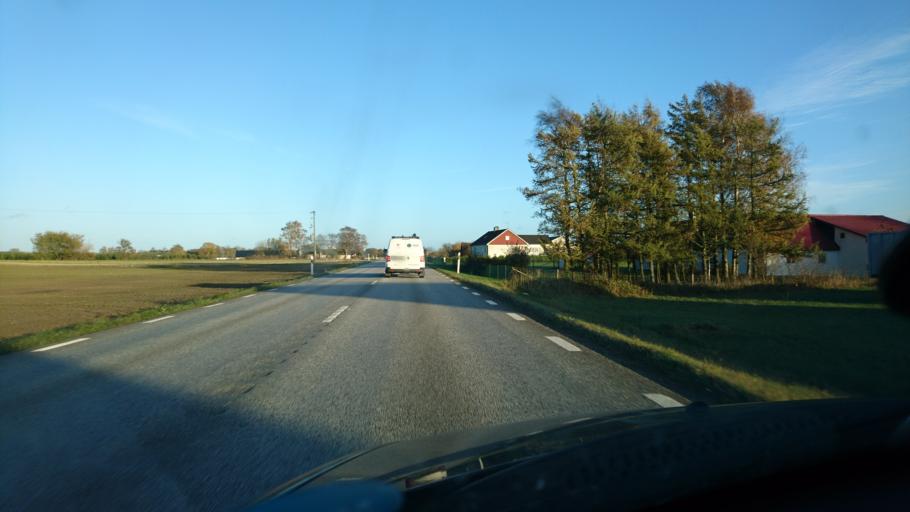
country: SE
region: Skane
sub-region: Tomelilla Kommun
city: Tomelilla
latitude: 55.5452
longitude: 14.0256
